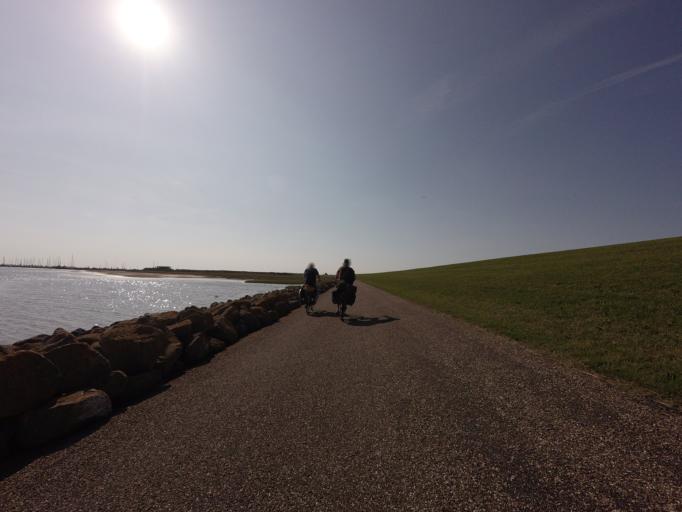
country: NL
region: Friesland
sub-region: Gemeente Schiermonnikoog
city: Schiermonnikoog
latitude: 53.4725
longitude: 6.1724
